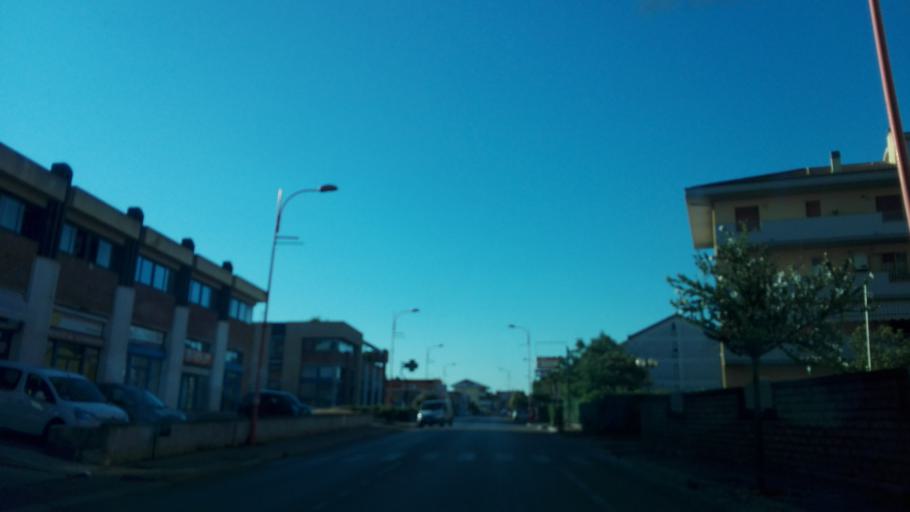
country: IT
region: Abruzzo
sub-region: Provincia di Pescara
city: Montesilvano Marina
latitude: 42.5011
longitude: 14.1656
